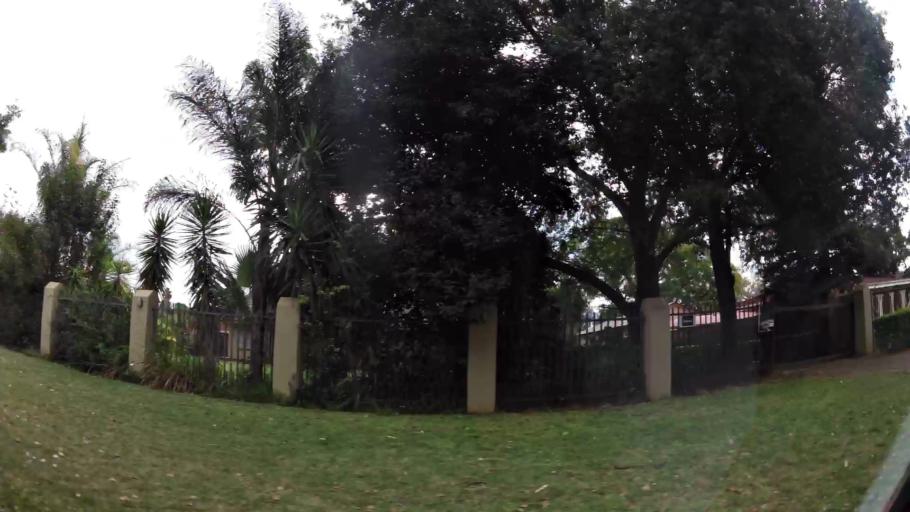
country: ZA
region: Limpopo
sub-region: Waterberg District Municipality
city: Modimolle
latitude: -24.5121
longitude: 28.7116
